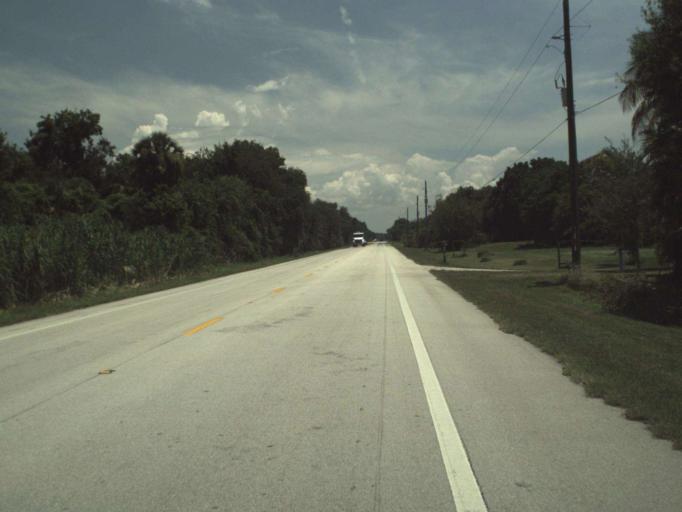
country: US
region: Florida
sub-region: Martin County
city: Indiantown
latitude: 27.0218
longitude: -80.6307
